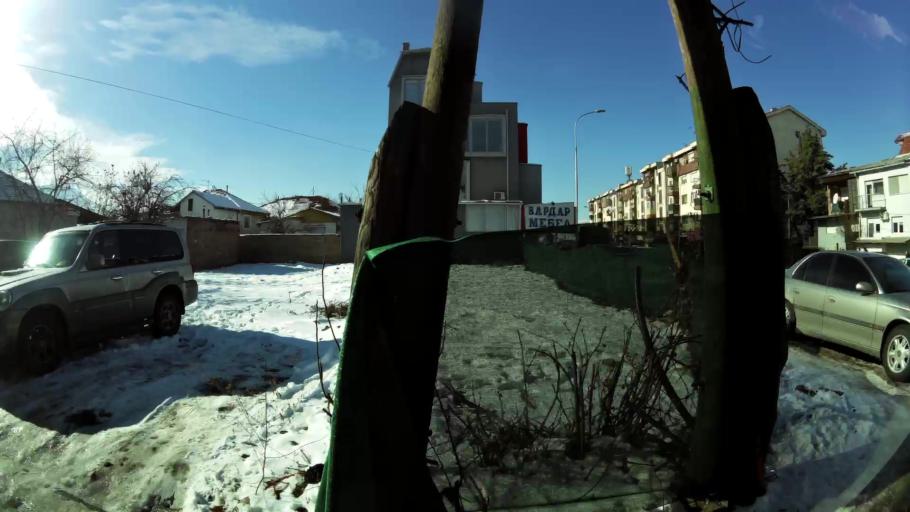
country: MK
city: Krushopek
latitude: 42.0064
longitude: 21.3566
